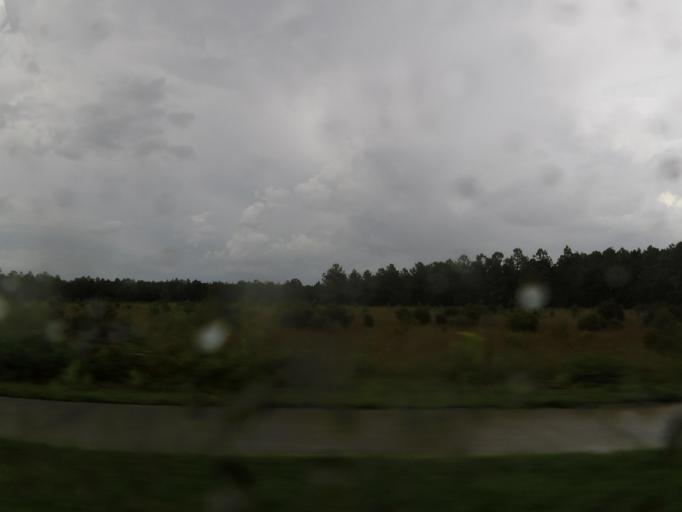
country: US
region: Florida
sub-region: Volusia County
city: Holly Hill
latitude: 29.2246
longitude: -81.1004
